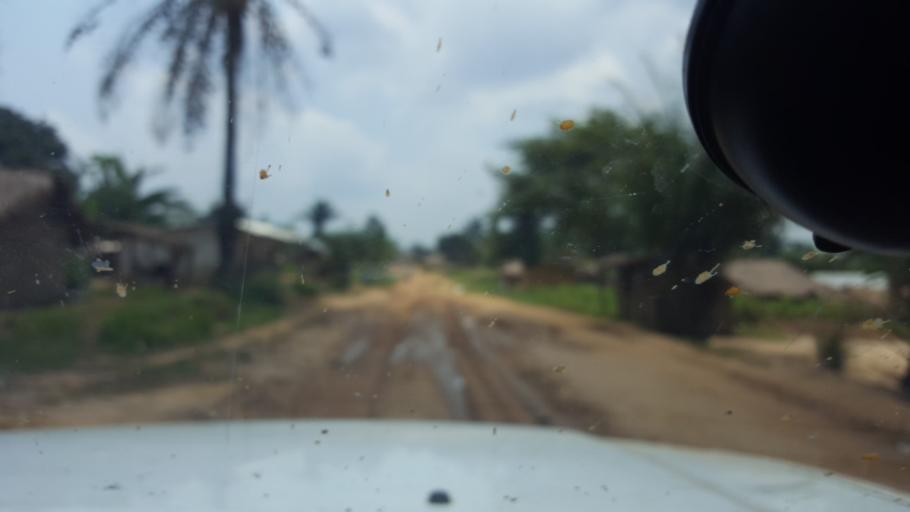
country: CD
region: Bandundu
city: Mushie
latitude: -3.7448
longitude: 16.6511
